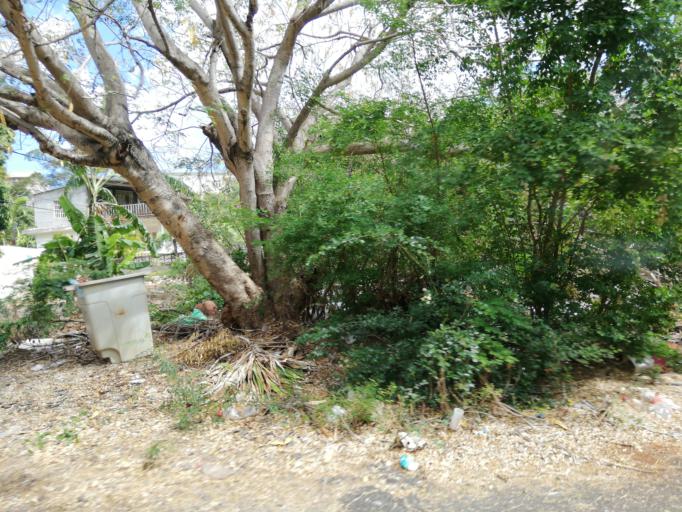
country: MU
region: Moka
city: Pailles
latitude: -20.1945
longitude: 57.4727
